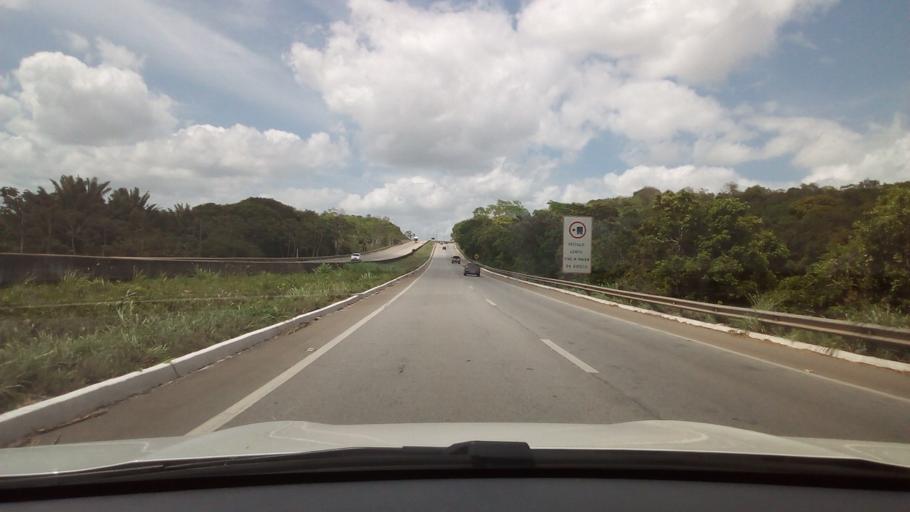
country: BR
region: Paraiba
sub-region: Mamanguape
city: Mamanguape
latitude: -6.9390
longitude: -35.0989
